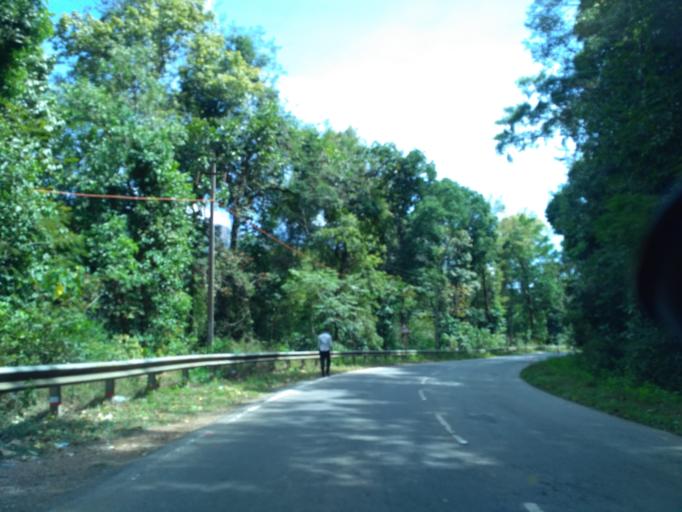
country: IN
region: Karnataka
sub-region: Kodagu
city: Madikeri
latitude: 12.4698
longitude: 75.6107
